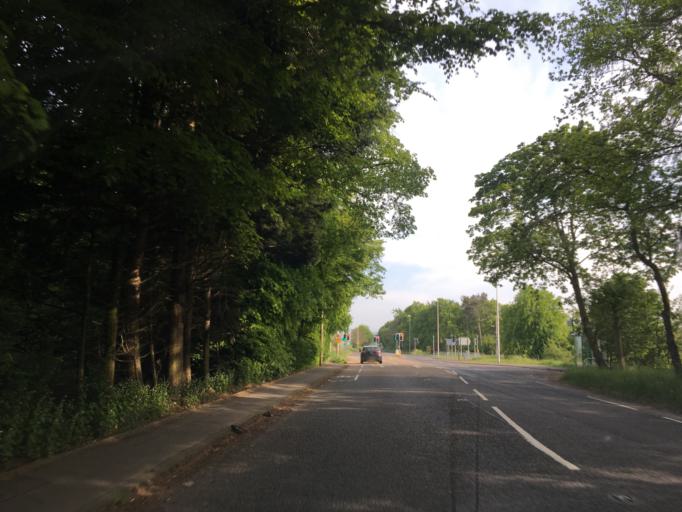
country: GB
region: Scotland
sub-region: Midlothian
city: Loanhead
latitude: 55.8702
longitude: -3.1910
